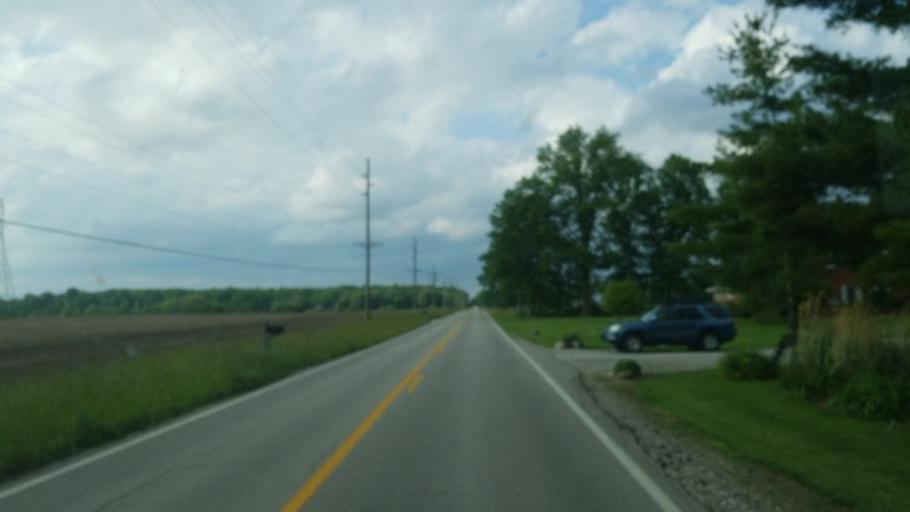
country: US
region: Ohio
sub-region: Delaware County
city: Sunbury
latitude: 40.2680
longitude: -82.7873
